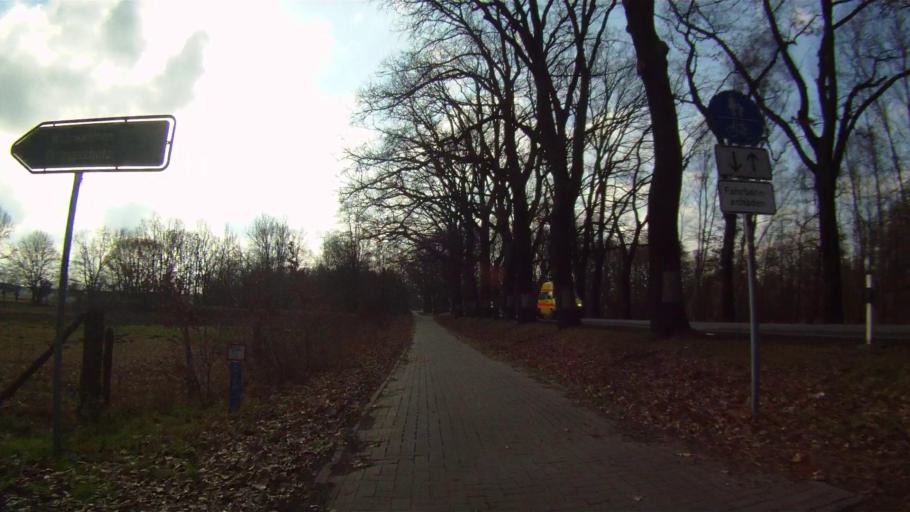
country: DE
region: Brandenburg
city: Erkner
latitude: 52.4034
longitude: 13.7483
